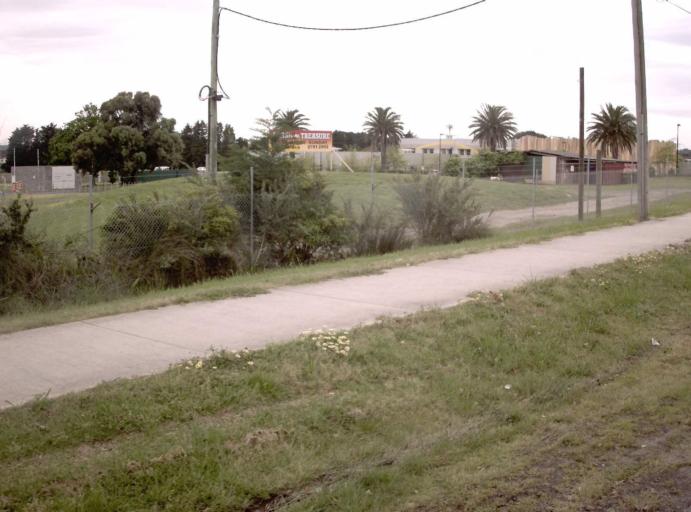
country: AU
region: Victoria
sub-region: Knox
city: Wantirna
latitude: -37.8502
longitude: 145.2250
